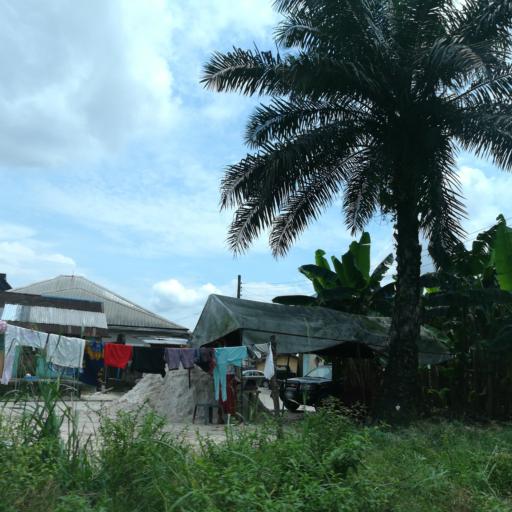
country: NG
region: Rivers
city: Port Harcourt
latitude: 4.7750
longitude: 7.0433
